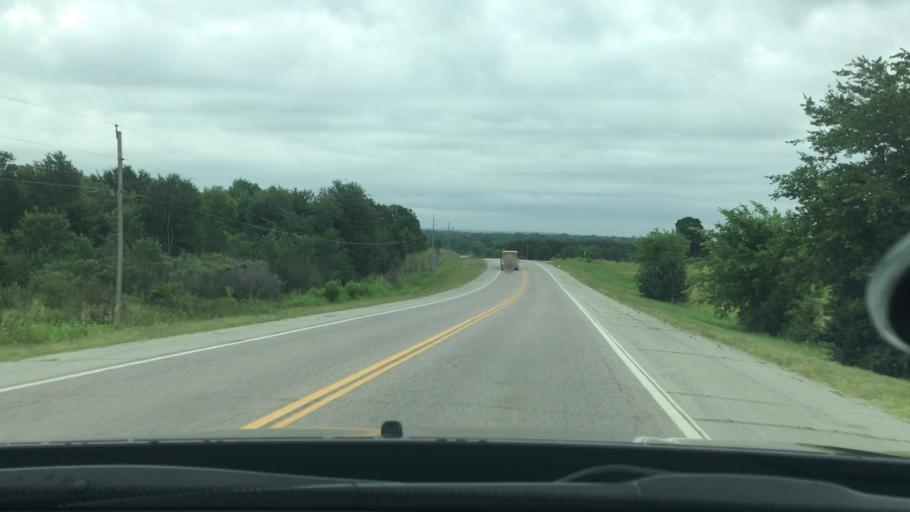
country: US
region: Oklahoma
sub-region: Coal County
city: Coalgate
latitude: 34.5548
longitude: -96.2394
